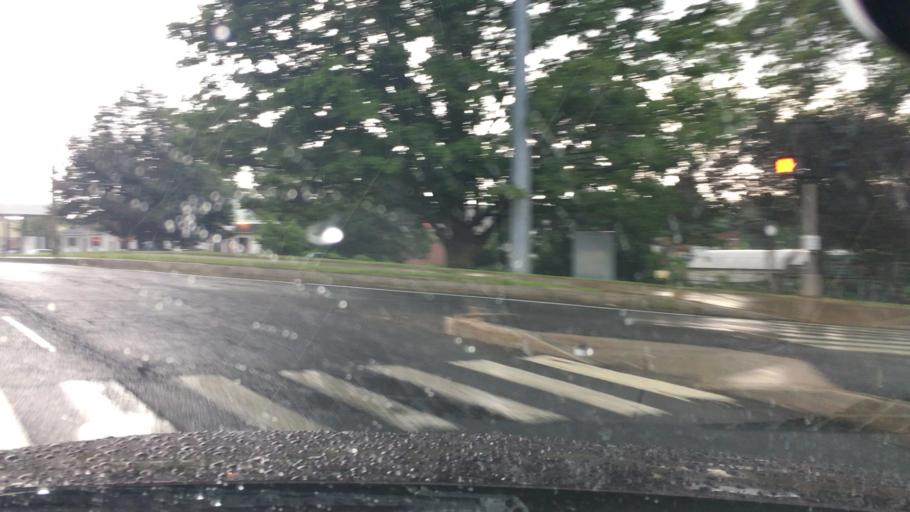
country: US
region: Connecticut
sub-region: Hartford County
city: Manchester
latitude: 41.7962
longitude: -72.5511
